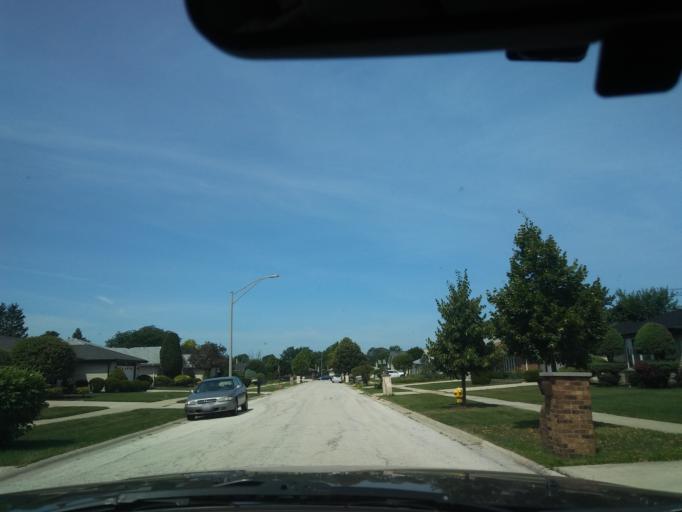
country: US
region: Illinois
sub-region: Cook County
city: Tinley Park
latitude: 41.6083
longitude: -87.7979
